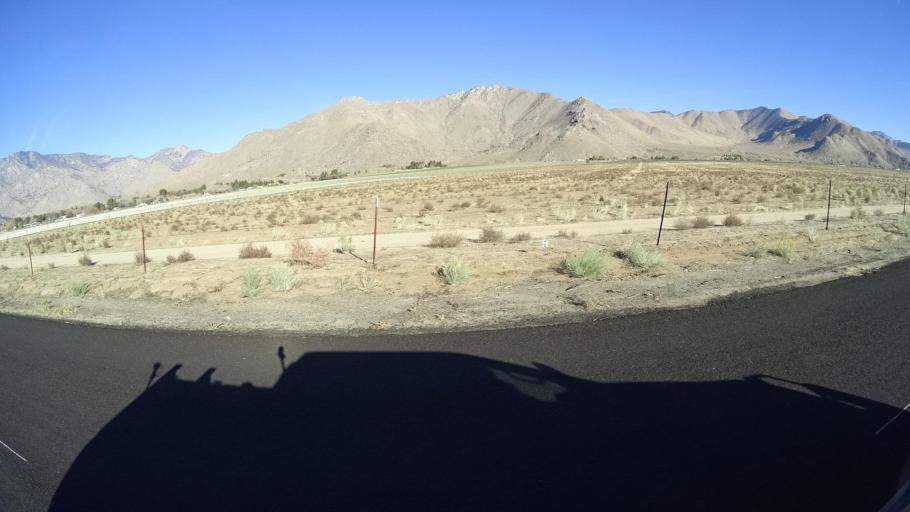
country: US
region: California
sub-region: Kern County
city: Weldon
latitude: 35.6442
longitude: -118.2711
